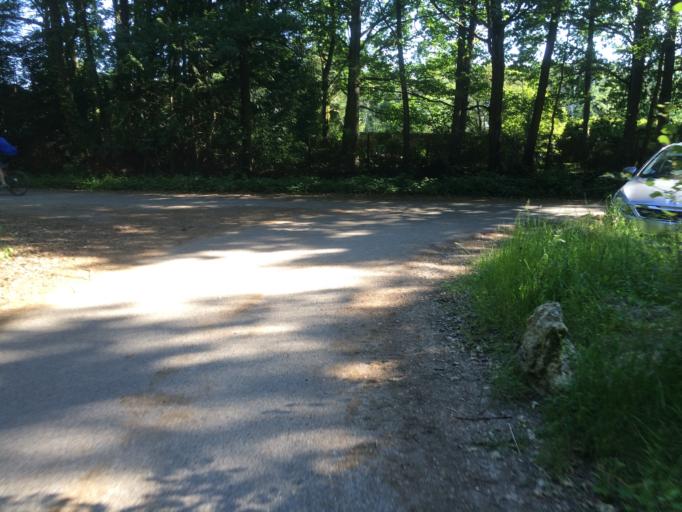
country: FR
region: Ile-de-France
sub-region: Departement du Val-de-Marne
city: Sucy-en-Brie
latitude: 48.7494
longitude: 2.5430
